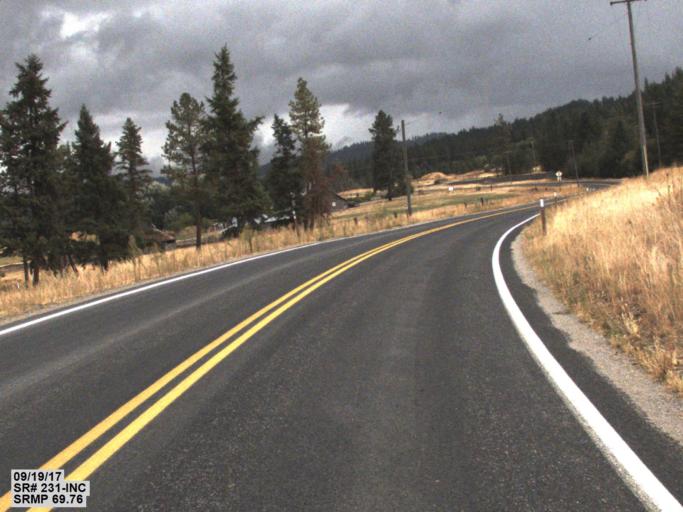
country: US
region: Washington
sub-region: Stevens County
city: Chewelah
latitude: 48.1469
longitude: -117.7278
